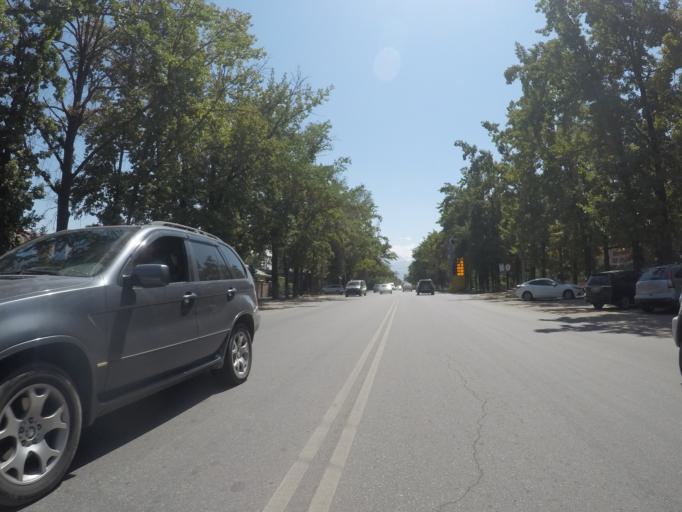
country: KG
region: Chuy
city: Bishkek
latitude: 42.8495
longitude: 74.5770
